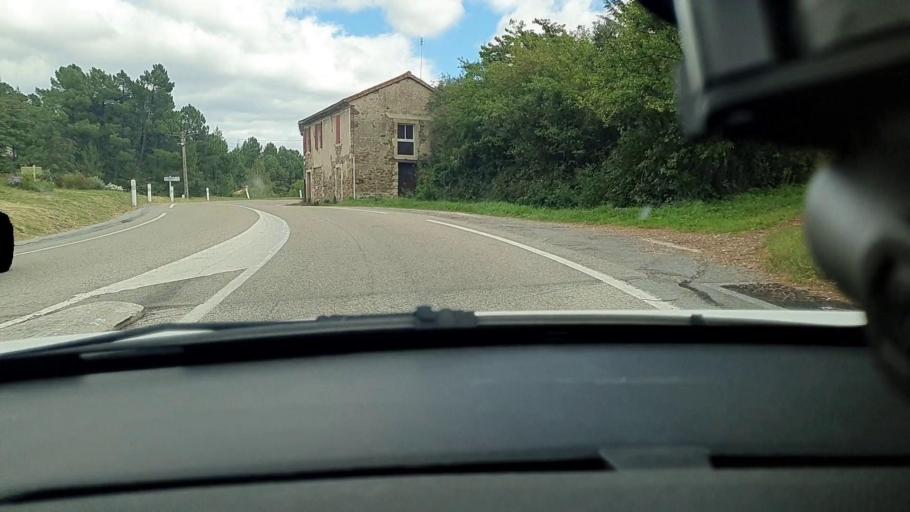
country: FR
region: Languedoc-Roussillon
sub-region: Departement du Gard
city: Branoux-les-Taillades
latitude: 44.2855
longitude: 3.9952
